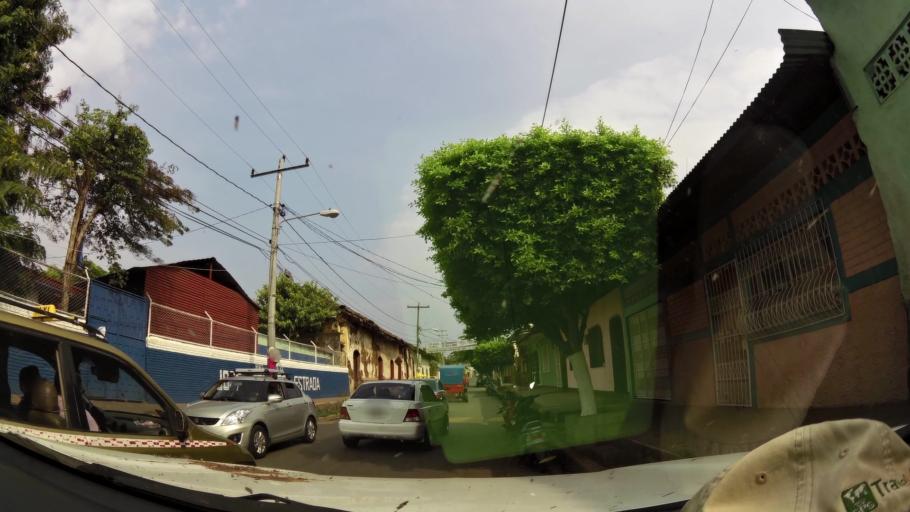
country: NI
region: Masaya
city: Masaya
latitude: 11.9763
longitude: -86.0984
